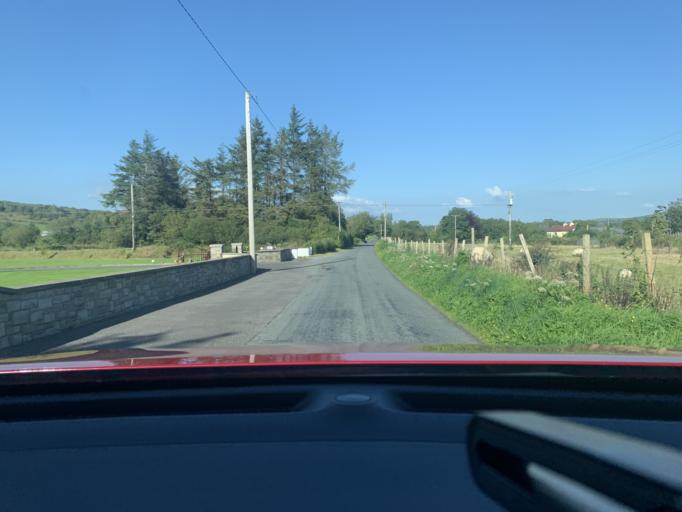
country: IE
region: Connaught
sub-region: Sligo
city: Tobercurry
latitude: 54.1207
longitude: -8.7509
